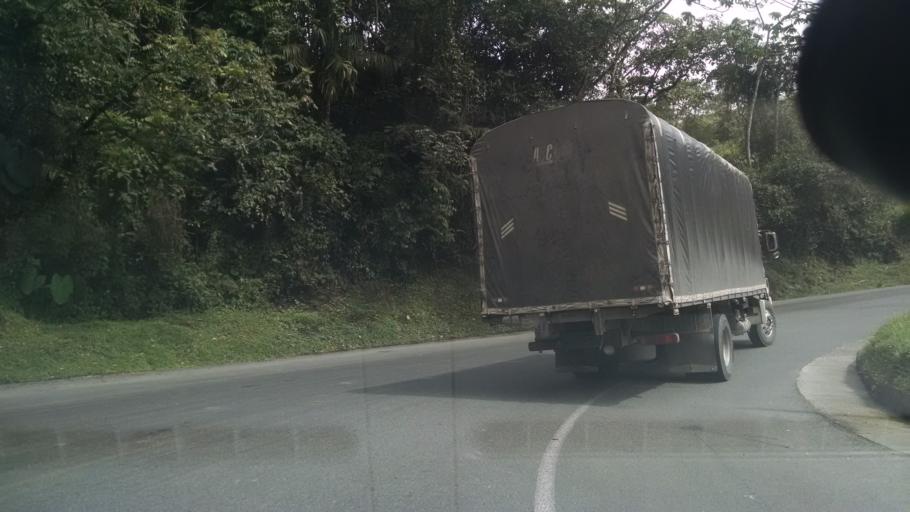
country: CO
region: Antioquia
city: Caldas
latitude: 6.0349
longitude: -75.6244
